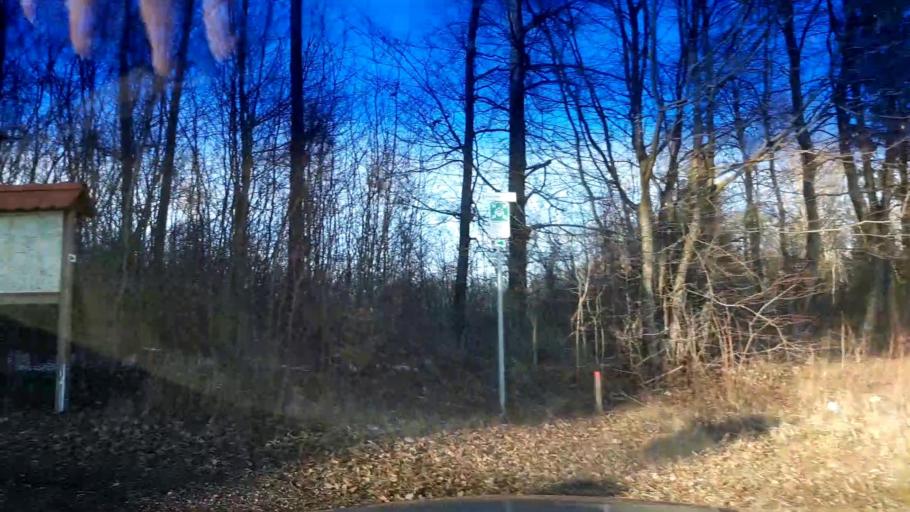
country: DE
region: Bavaria
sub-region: Upper Franconia
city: Heiligenstadt
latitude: 49.8566
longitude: 11.1509
